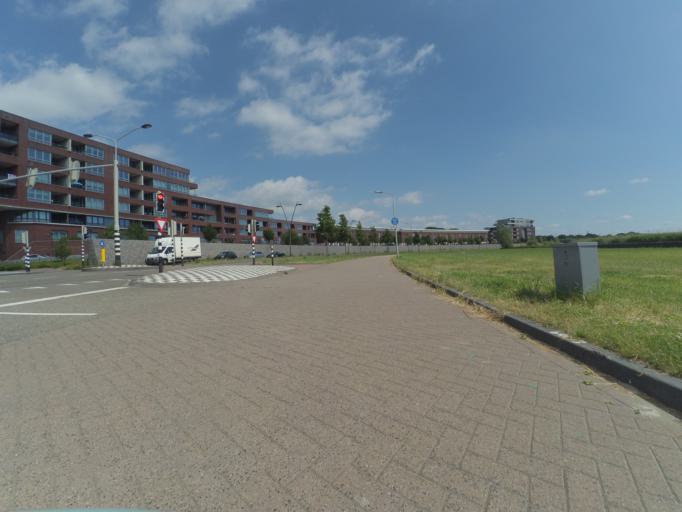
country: NL
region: North Brabant
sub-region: Gemeente Bergen op Zoom
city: Bergen op Zoom
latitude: 51.4761
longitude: 4.2983
